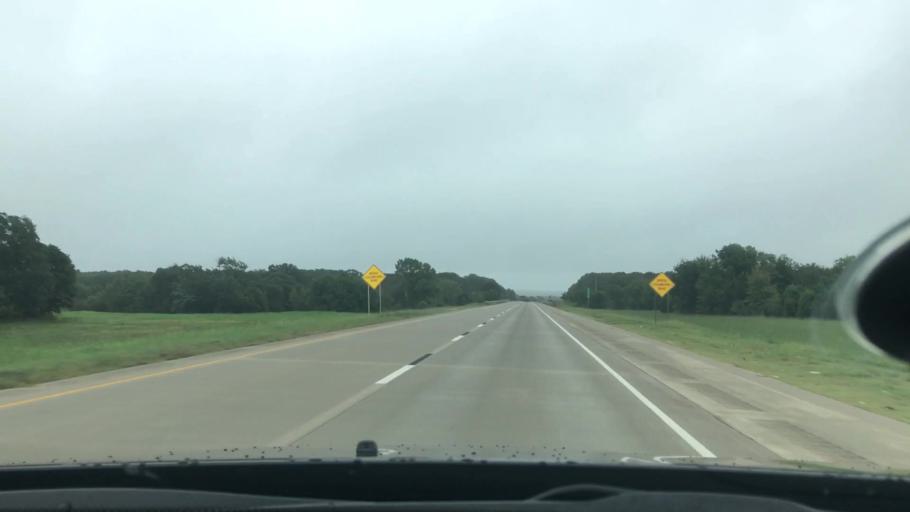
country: US
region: Oklahoma
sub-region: Okfuskee County
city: Boley
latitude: 35.3840
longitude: -96.5689
